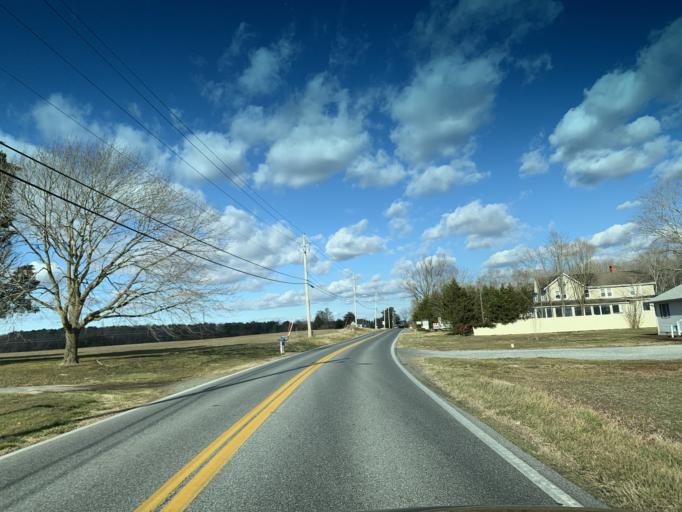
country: US
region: Maryland
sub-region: Worcester County
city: Berlin
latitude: 38.3362
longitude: -75.2208
